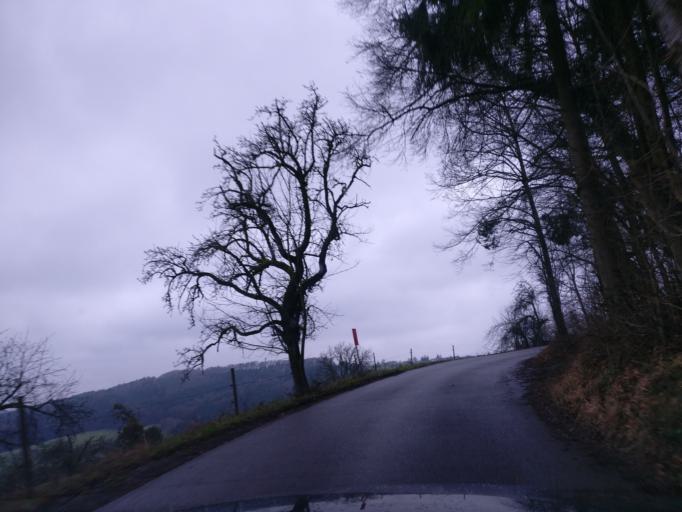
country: DE
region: Baden-Wuerttemberg
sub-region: Regierungsbezirk Stuttgart
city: Rudersberg
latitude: 48.8772
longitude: 9.5003
